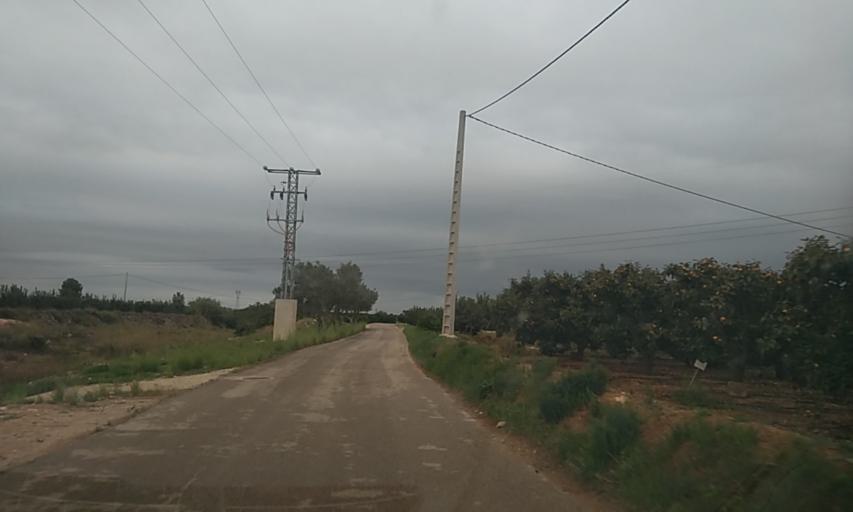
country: ES
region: Valencia
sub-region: Provincia de Valencia
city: Benimodo
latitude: 39.1881
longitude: -0.5498
